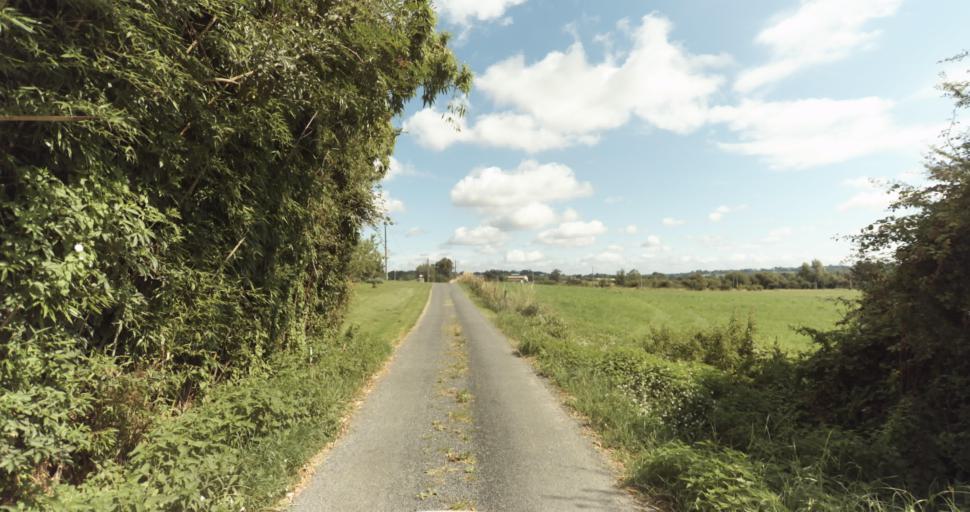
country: FR
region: Aquitaine
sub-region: Departement de la Gironde
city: Bazas
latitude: 44.4403
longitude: -0.1764
